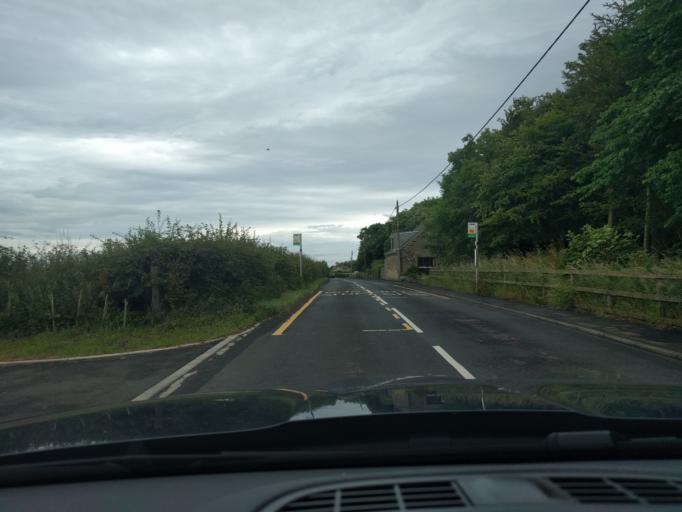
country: GB
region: England
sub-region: Northumberland
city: Cresswell
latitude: 55.2309
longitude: -1.5506
